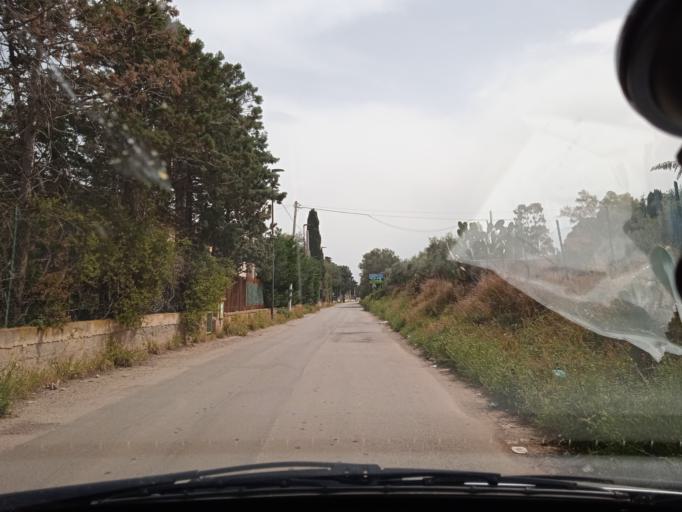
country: IT
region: Sicily
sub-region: Palermo
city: Torre Colonna-Sperone
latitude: 38.0236
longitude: 13.5788
